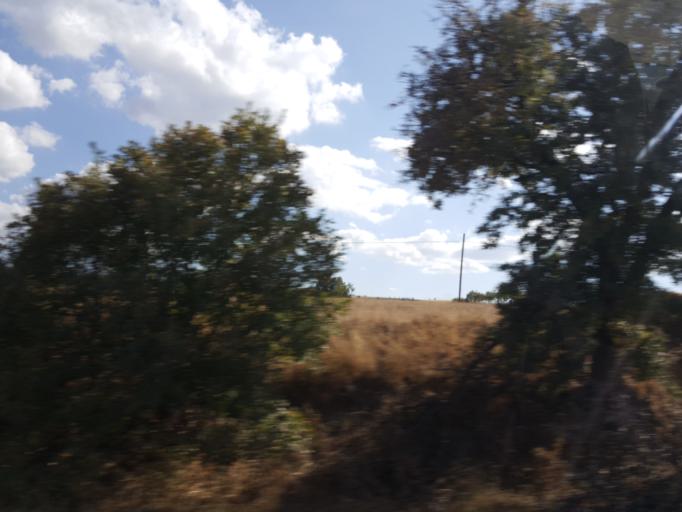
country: TR
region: Tokat
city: Sulusaray
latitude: 40.0025
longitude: 36.1343
